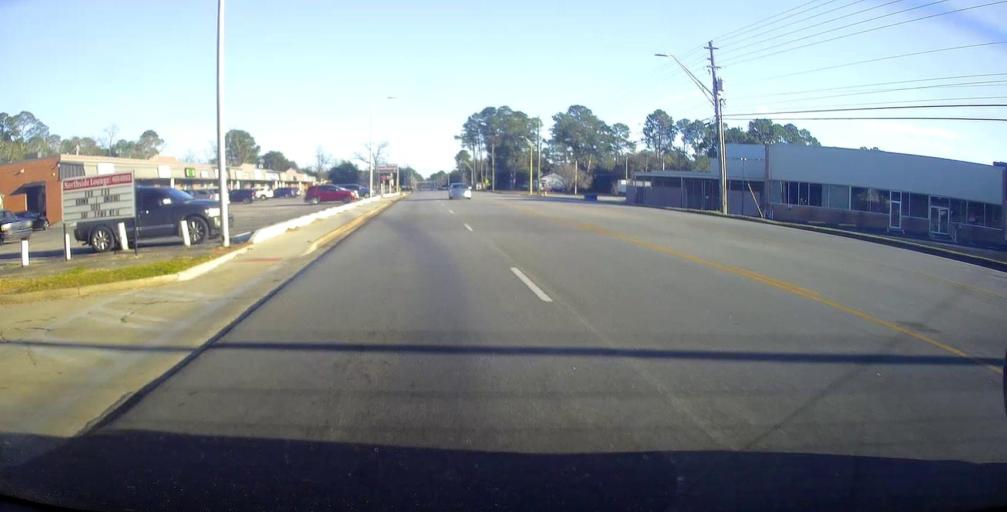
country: US
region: Georgia
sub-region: Dougherty County
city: Albany
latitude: 31.6090
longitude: -84.1742
